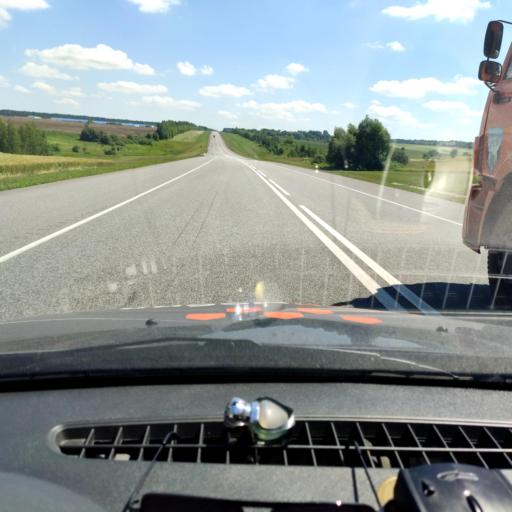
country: RU
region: Orjol
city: Zmiyevka
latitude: 52.8208
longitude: 36.2790
